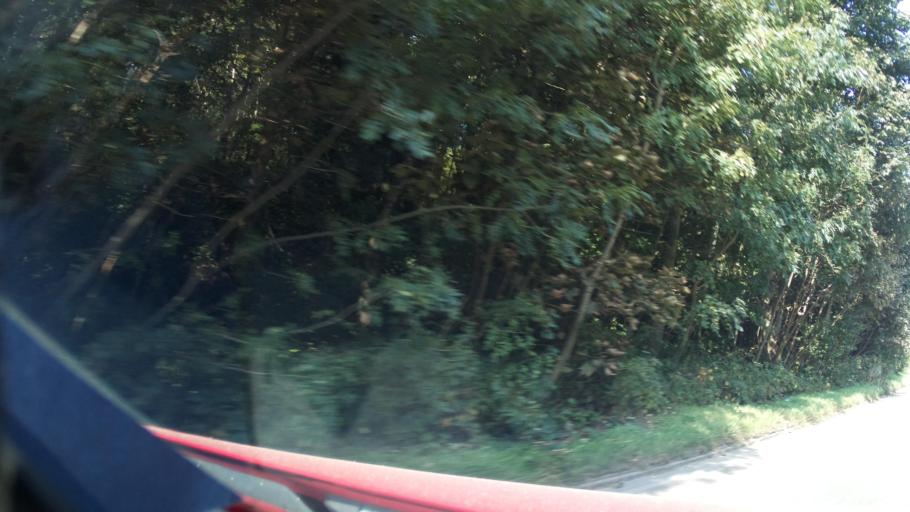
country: GB
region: England
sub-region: Walsall
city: Brownhills
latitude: 52.6306
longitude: -1.9089
